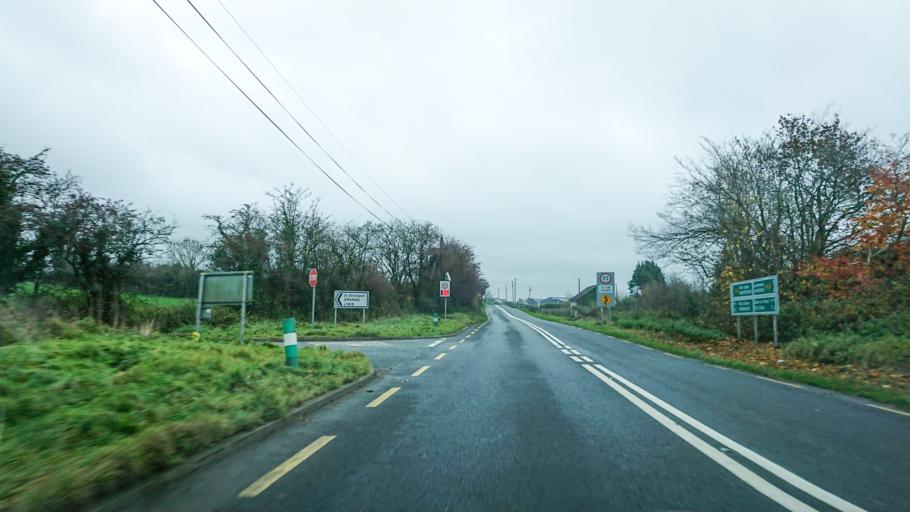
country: IE
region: Leinster
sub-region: Kilkenny
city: Mooncoin
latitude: 52.3056
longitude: -7.2795
